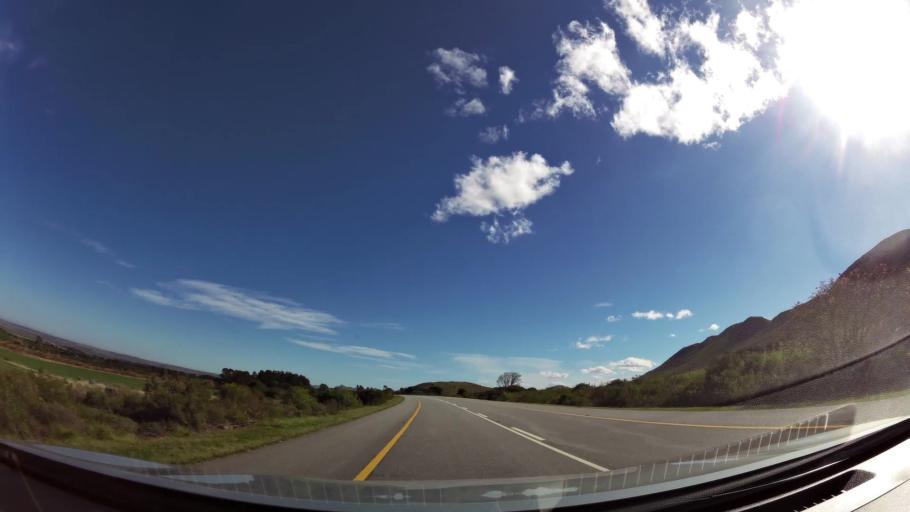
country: ZA
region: Eastern Cape
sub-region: Cacadu District Municipality
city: Kruisfontein
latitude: -33.9939
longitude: 24.6974
